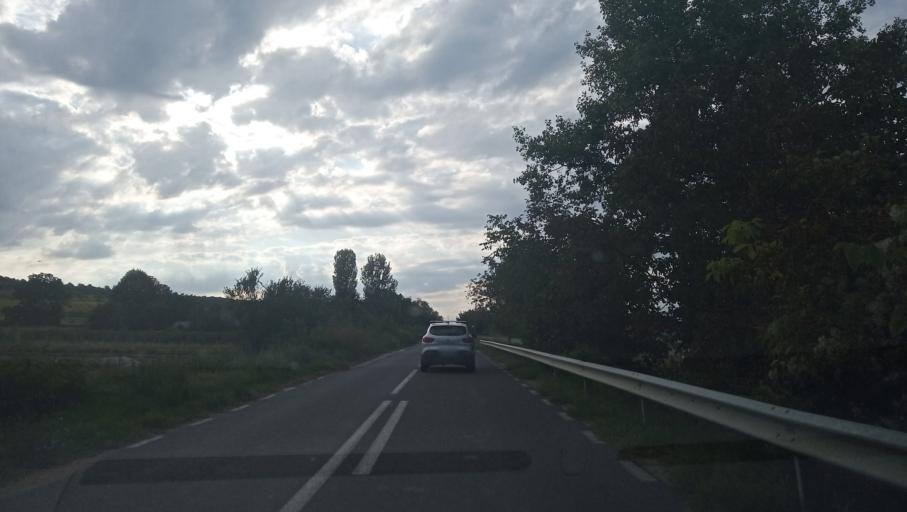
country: RO
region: Constanta
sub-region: Comuna Ostrov
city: Ostrov
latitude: 44.1098
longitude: 27.3521
